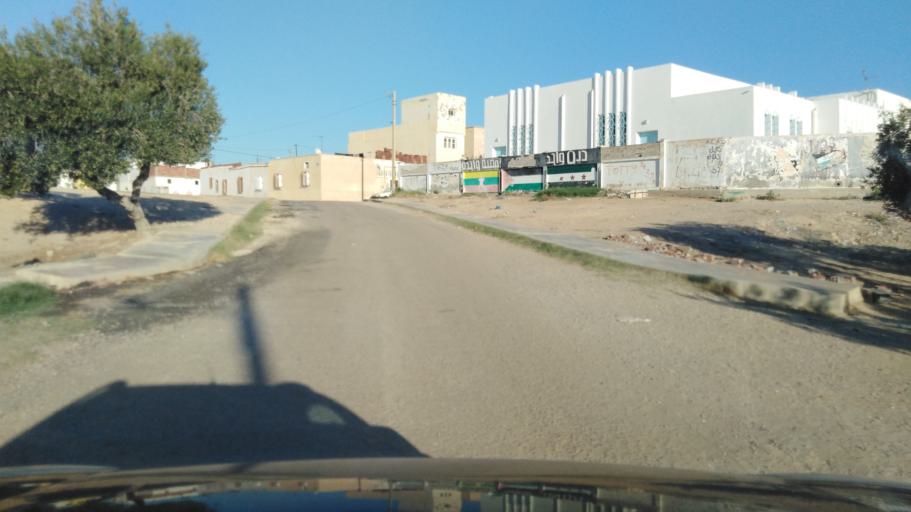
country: TN
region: Qabis
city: Gabes
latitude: 33.9540
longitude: 10.0111
